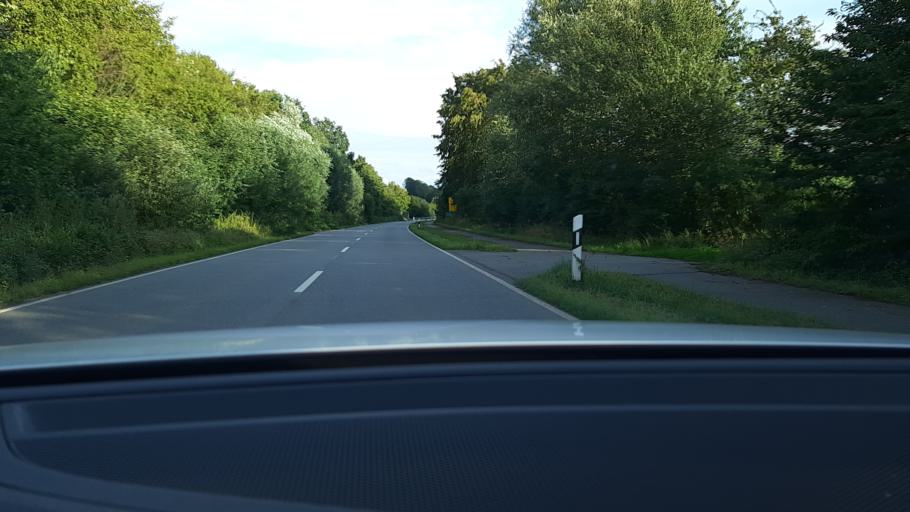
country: DE
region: Schleswig-Holstein
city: Monkhagen
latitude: 53.9074
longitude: 10.5456
